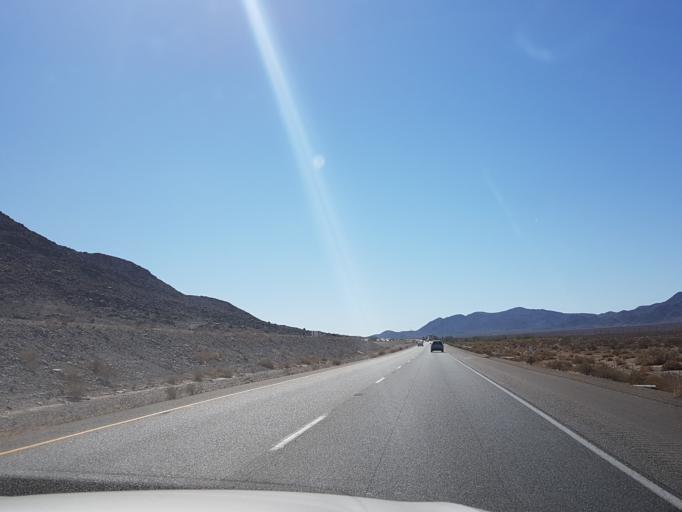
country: US
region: California
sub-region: San Bernardino County
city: Fort Irwin
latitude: 35.1919
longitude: -116.1560
